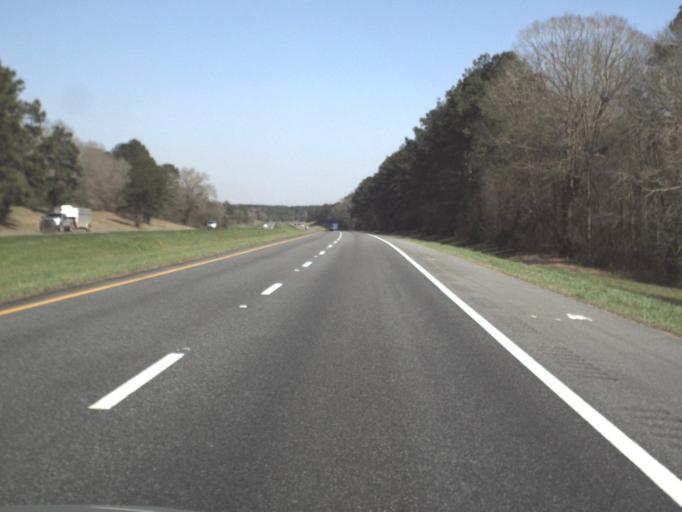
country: US
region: Florida
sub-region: Jackson County
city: Marianna
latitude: 30.7556
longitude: -85.3544
